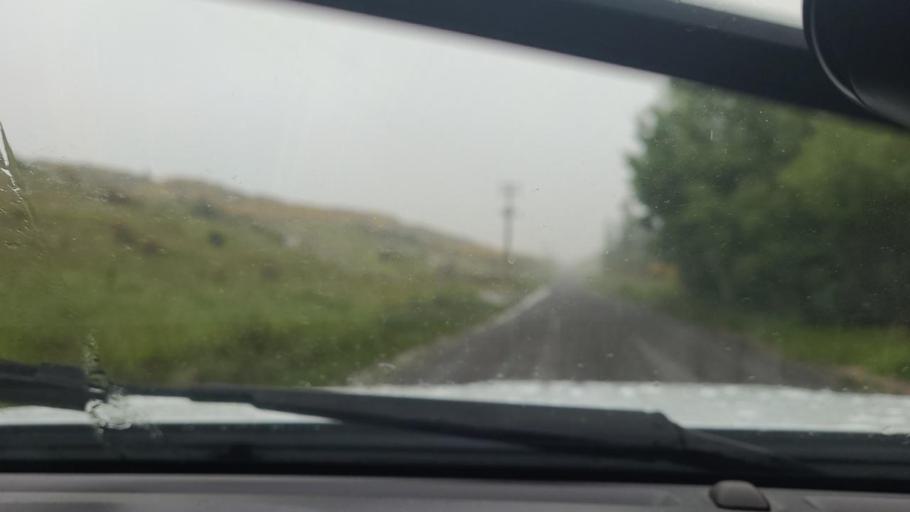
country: NZ
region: Southland
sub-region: Southland District
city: Riverton
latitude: -45.9122
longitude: 167.9604
